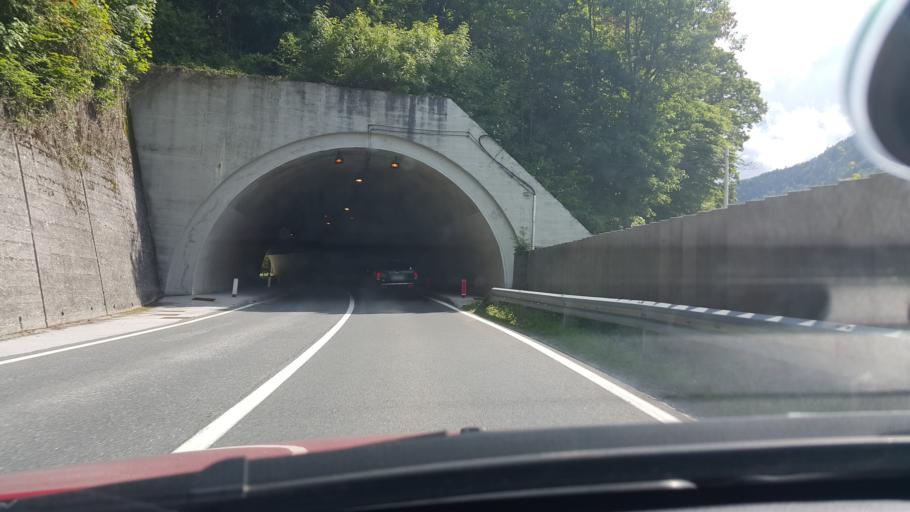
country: SI
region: Trzic
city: Bistrica pri Trzicu
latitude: 46.3606
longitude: 14.3002
